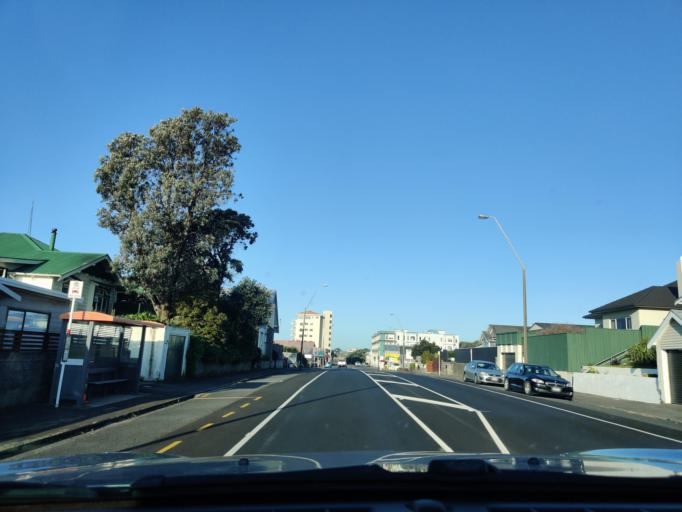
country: NZ
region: Taranaki
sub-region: New Plymouth District
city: New Plymouth
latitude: -39.0577
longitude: 174.0651
